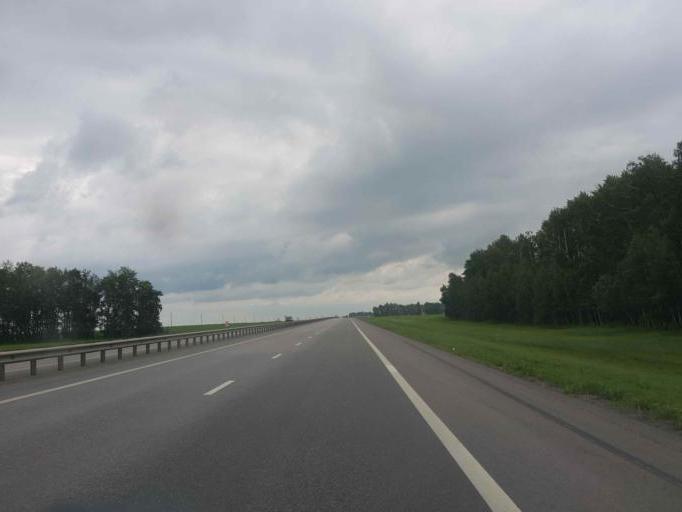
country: RU
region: Tambov
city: Zavoronezhskoye
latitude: 52.8318
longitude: 40.8819
